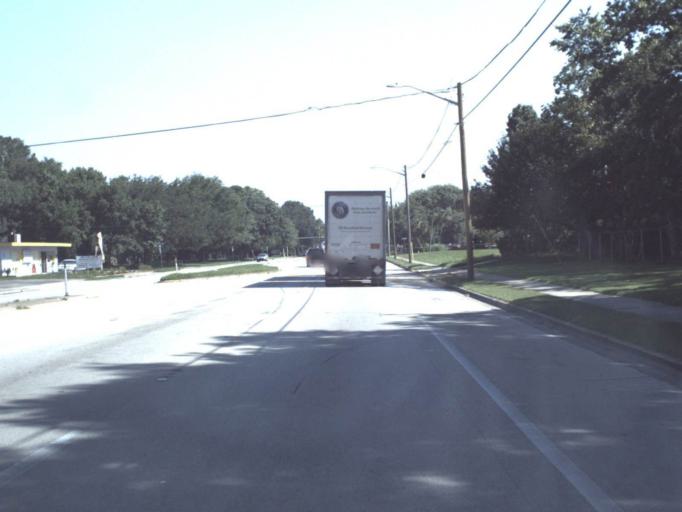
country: US
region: Florida
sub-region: Duval County
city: Jacksonville
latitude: 30.3436
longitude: -81.7312
